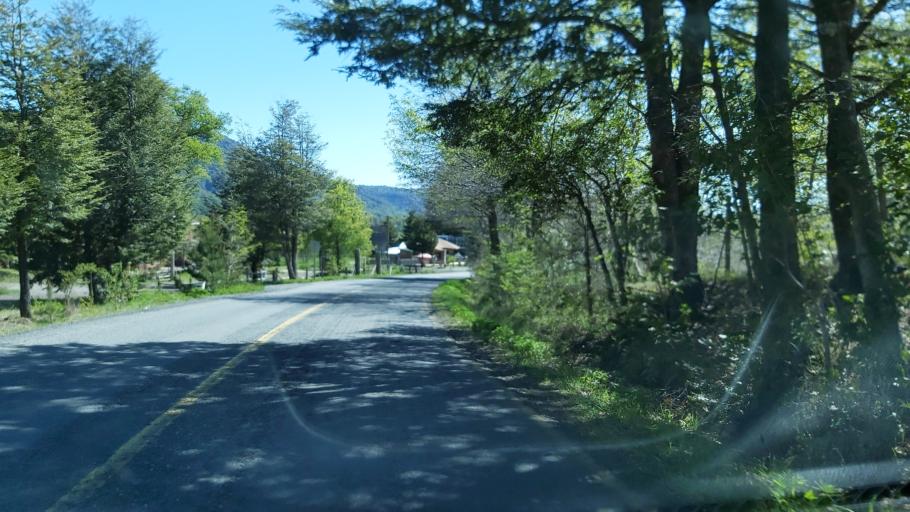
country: CL
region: Araucania
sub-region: Provincia de Cautin
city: Vilcun
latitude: -38.4782
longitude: -71.5346
